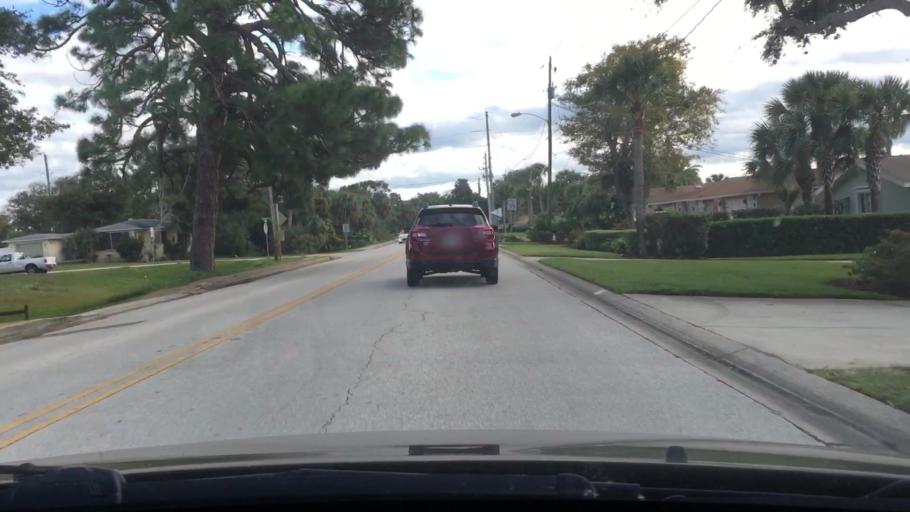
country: US
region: Florida
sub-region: Volusia County
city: Ormond Beach
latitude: 29.2786
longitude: -81.0423
